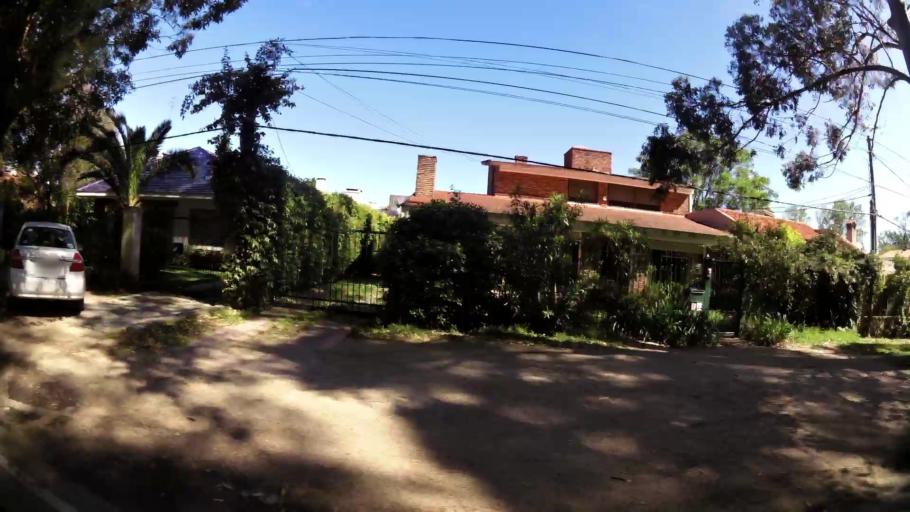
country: UY
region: Canelones
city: Barra de Carrasco
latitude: -34.8821
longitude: -56.0464
